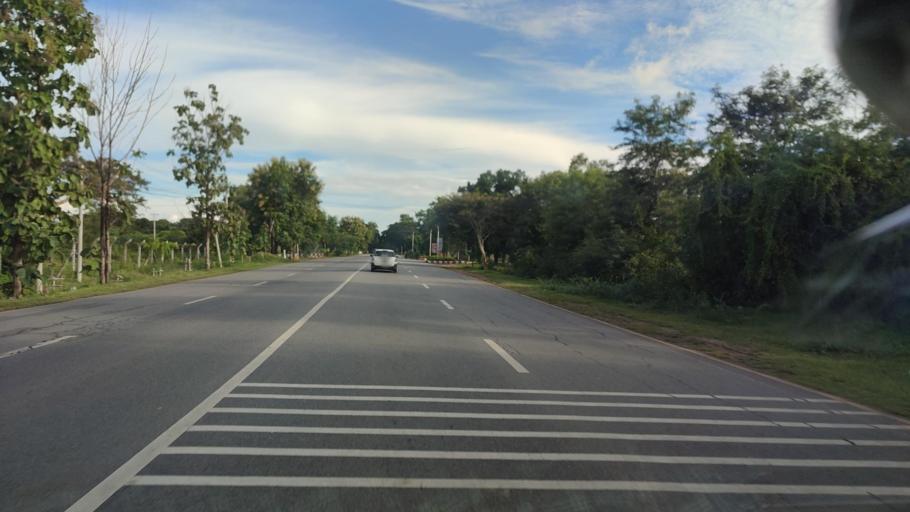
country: MM
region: Mandalay
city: Yamethin
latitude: 20.1539
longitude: 96.1919
